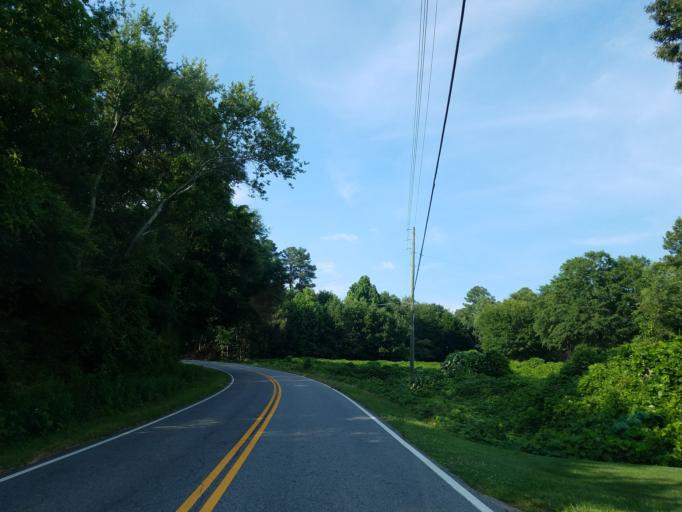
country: US
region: Georgia
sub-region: Forsyth County
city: Cumming
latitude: 34.2896
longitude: -84.0670
